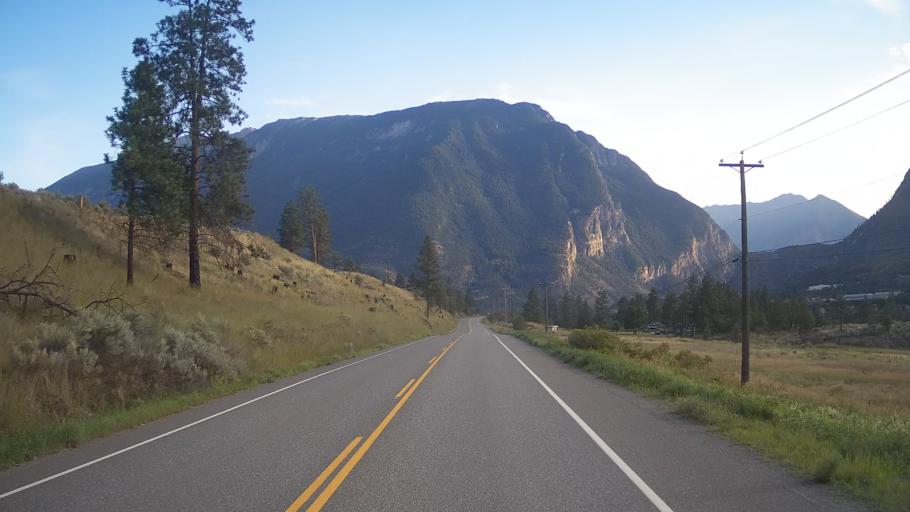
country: CA
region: British Columbia
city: Lillooet
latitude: 50.6979
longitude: -121.9171
